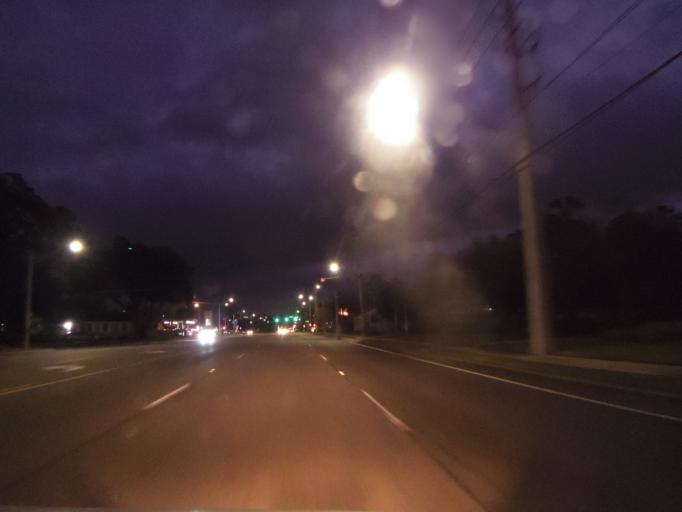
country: US
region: Florida
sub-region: Clay County
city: Bellair-Meadowbrook Terrace
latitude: 30.2472
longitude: -81.7326
